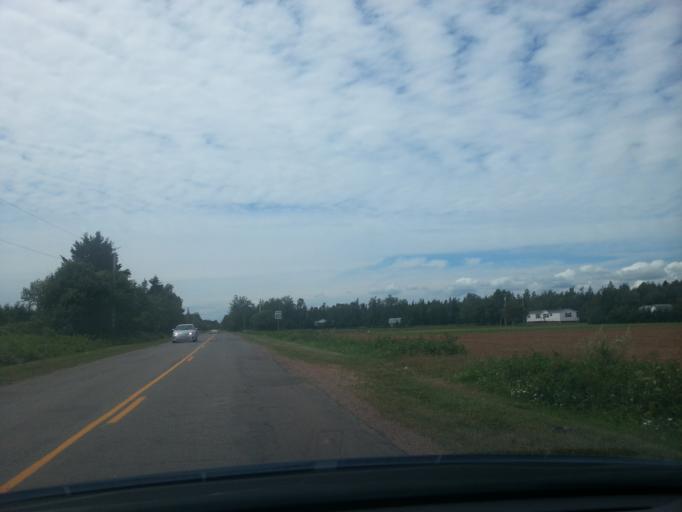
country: CA
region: Prince Edward Island
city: Summerside
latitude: 46.4048
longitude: -63.8469
